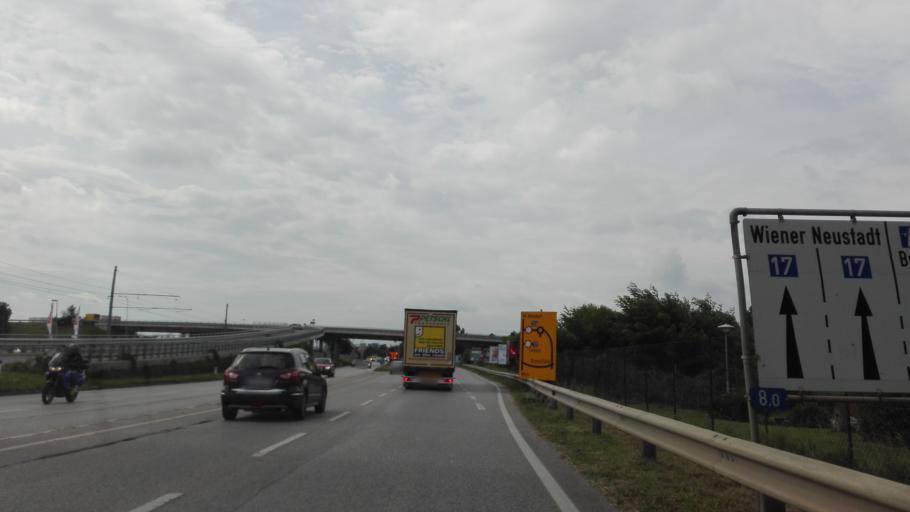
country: AT
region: Lower Austria
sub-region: Politischer Bezirk Modling
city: Vosendorf
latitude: 48.1158
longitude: 16.3162
